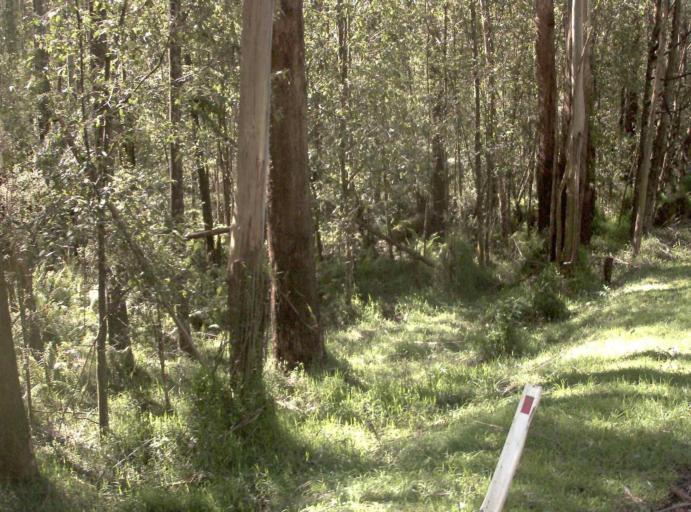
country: AU
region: Victoria
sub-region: Yarra Ranges
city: Millgrove
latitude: -37.8711
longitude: 145.8048
